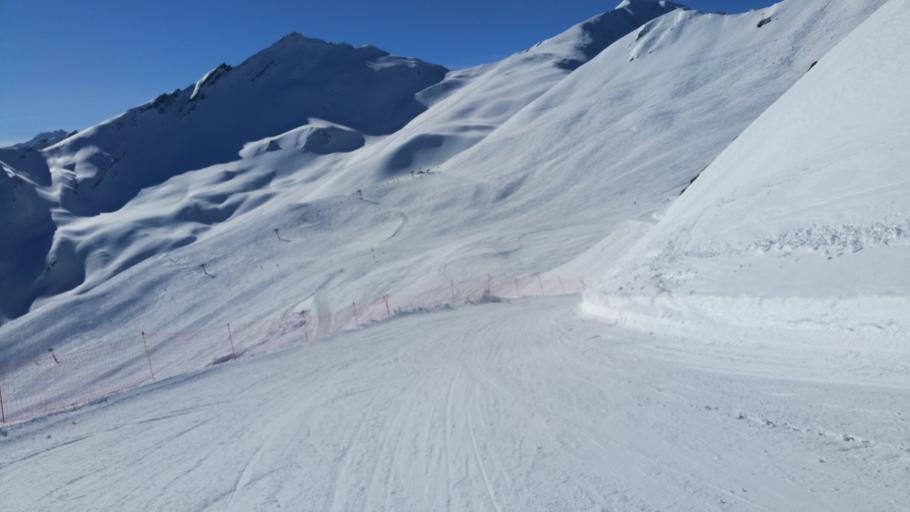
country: FR
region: Rhone-Alpes
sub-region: Departement de la Savoie
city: Valloire
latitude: 45.2055
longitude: 6.3934
